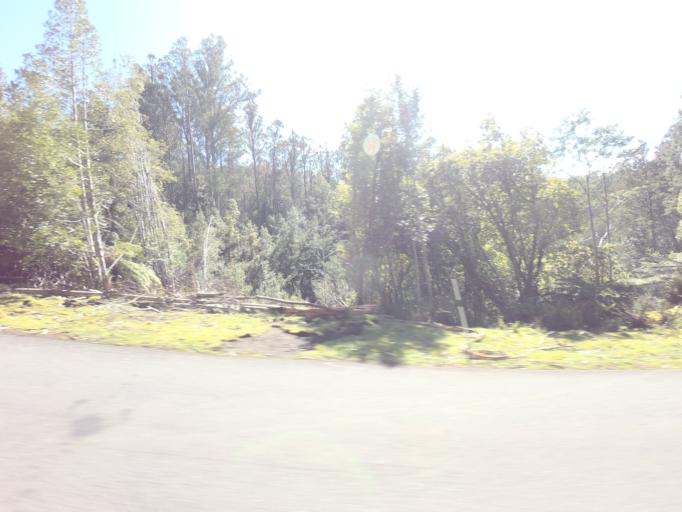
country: AU
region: Tasmania
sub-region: Derwent Valley
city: New Norfolk
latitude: -42.7469
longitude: 146.5011
